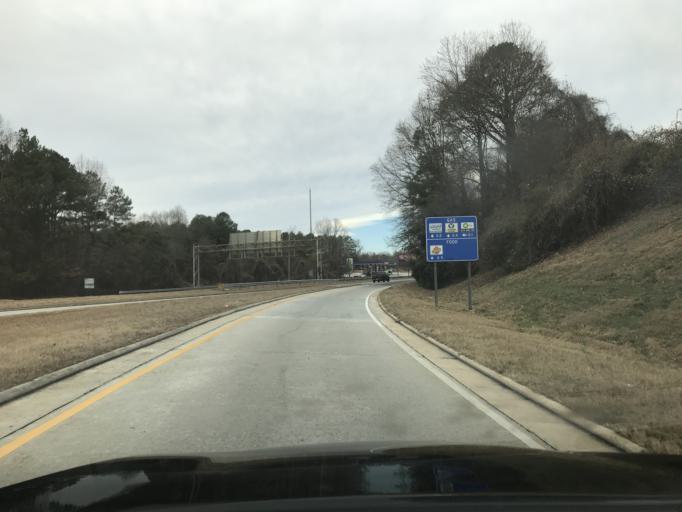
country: US
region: Georgia
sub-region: Fulton County
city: East Point
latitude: 33.6906
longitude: -84.5026
